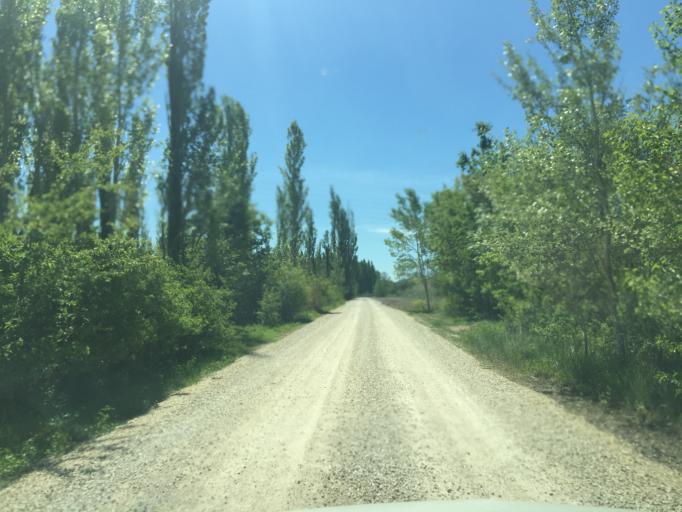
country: FR
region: Languedoc-Roussillon
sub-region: Departement du Gard
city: Montfaucon
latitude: 44.0836
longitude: 4.7712
